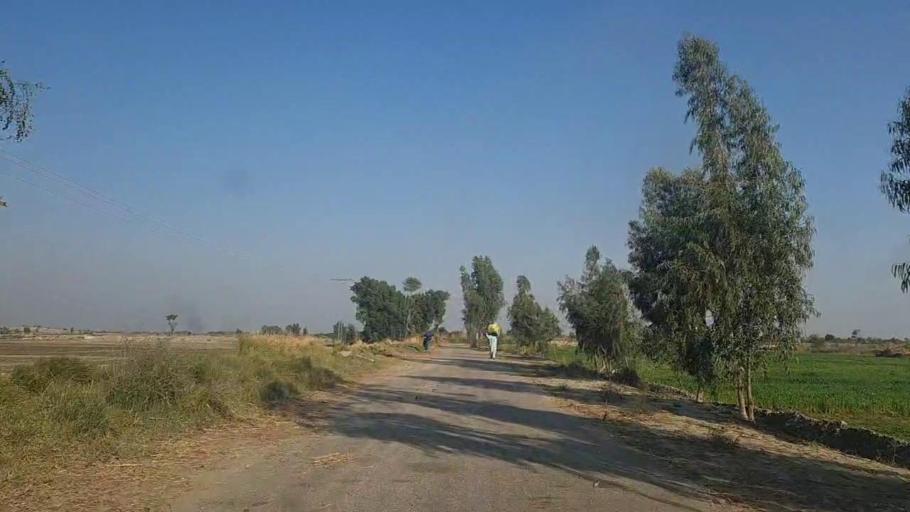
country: PK
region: Sindh
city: Jam Sahib
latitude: 26.3351
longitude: 68.7594
